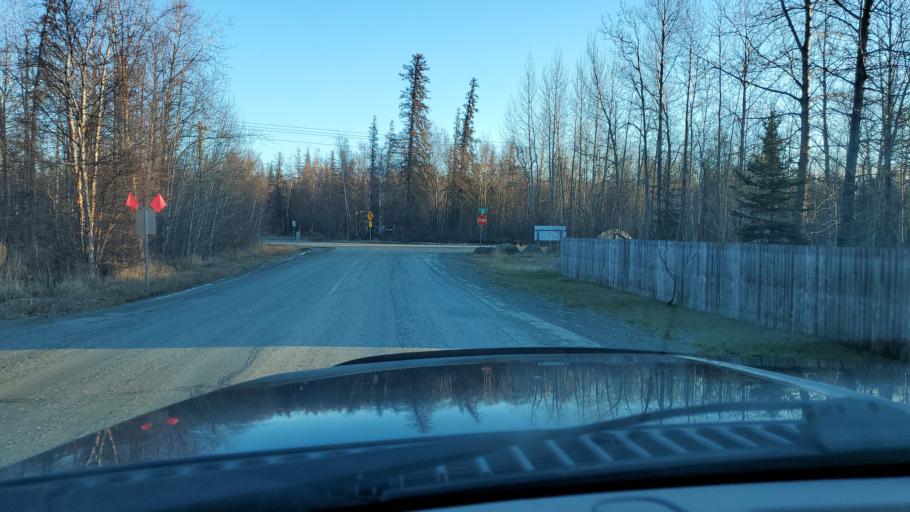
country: US
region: Alaska
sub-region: Matanuska-Susitna Borough
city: Gateway
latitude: 61.5885
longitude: -149.2478
